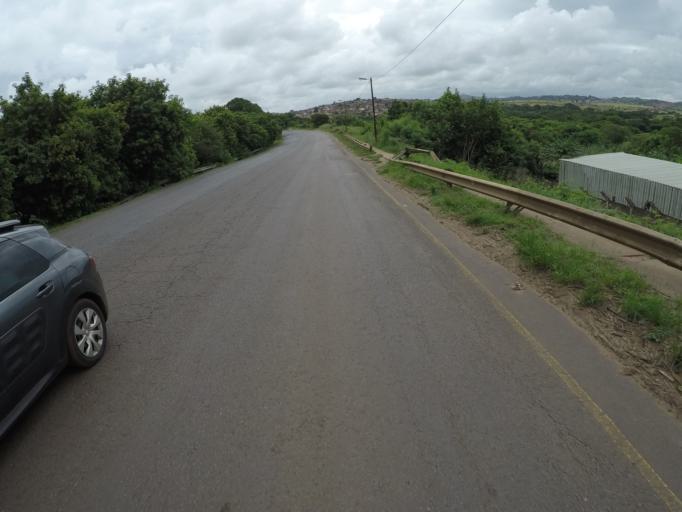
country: ZA
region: KwaZulu-Natal
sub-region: uThungulu District Municipality
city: Empangeni
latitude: -28.7758
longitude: 31.8899
